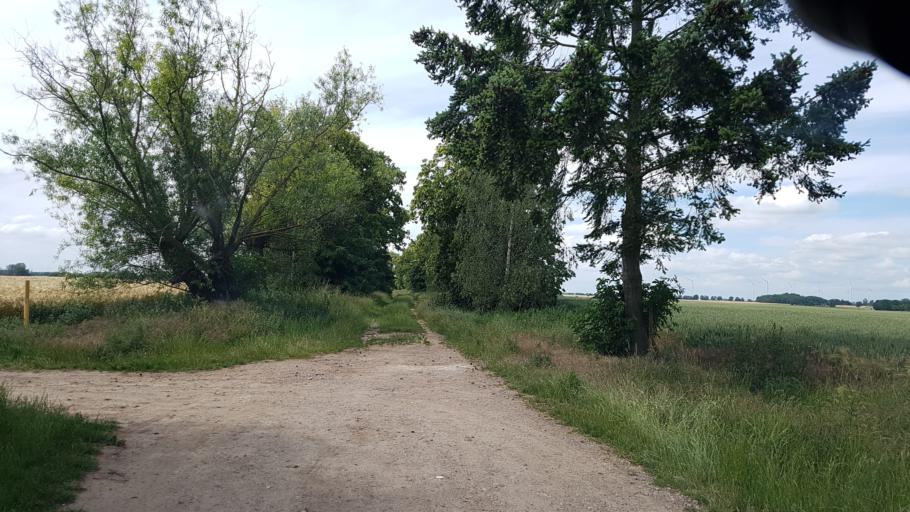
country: DE
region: Mecklenburg-Vorpommern
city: Strasburg
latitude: 53.4449
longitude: 13.8056
